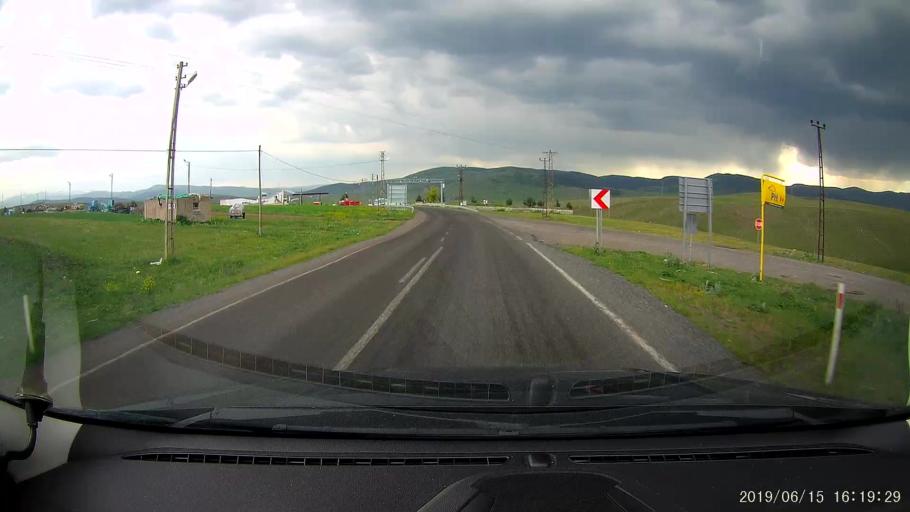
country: TR
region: Ardahan
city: Hanak
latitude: 41.2280
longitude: 42.8500
